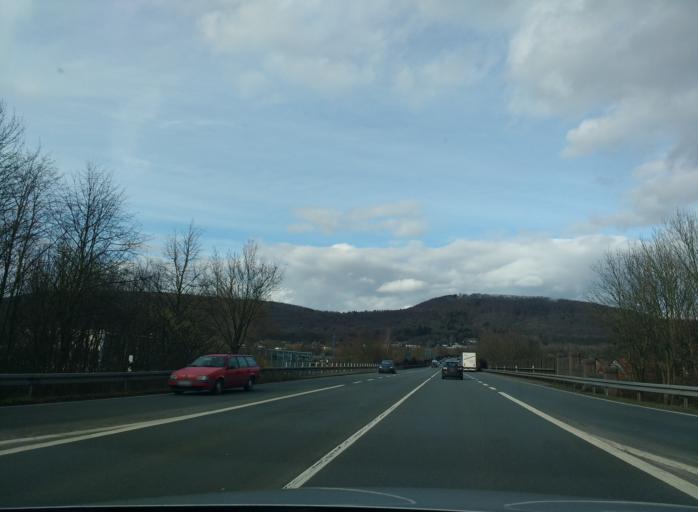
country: DE
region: Lower Saxony
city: Rinteln
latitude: 52.1964
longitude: 9.0949
